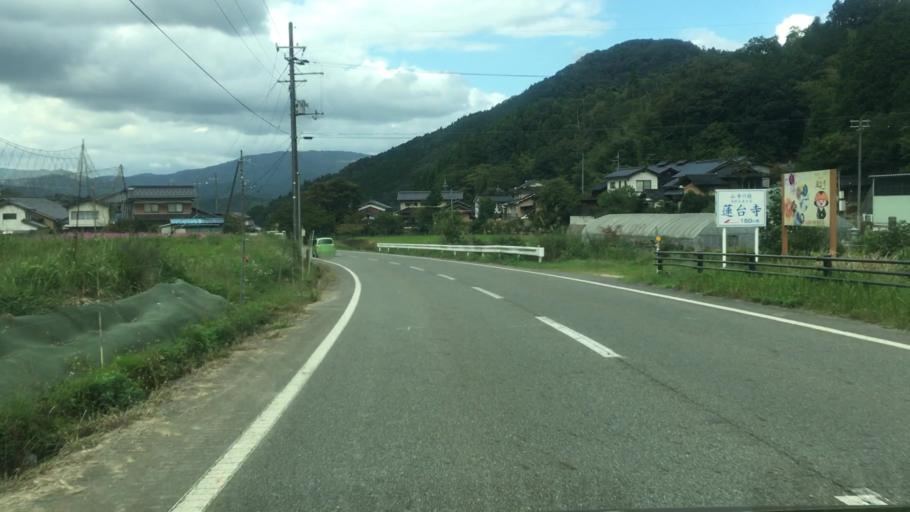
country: JP
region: Hyogo
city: Toyooka
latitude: 35.4348
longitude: 134.7351
